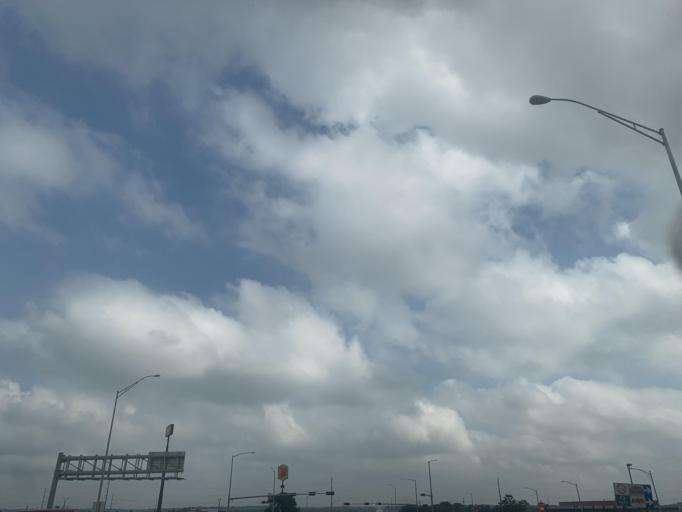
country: US
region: Nebraska
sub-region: Sarpy County
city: Chalco
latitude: 41.1643
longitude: -96.1388
